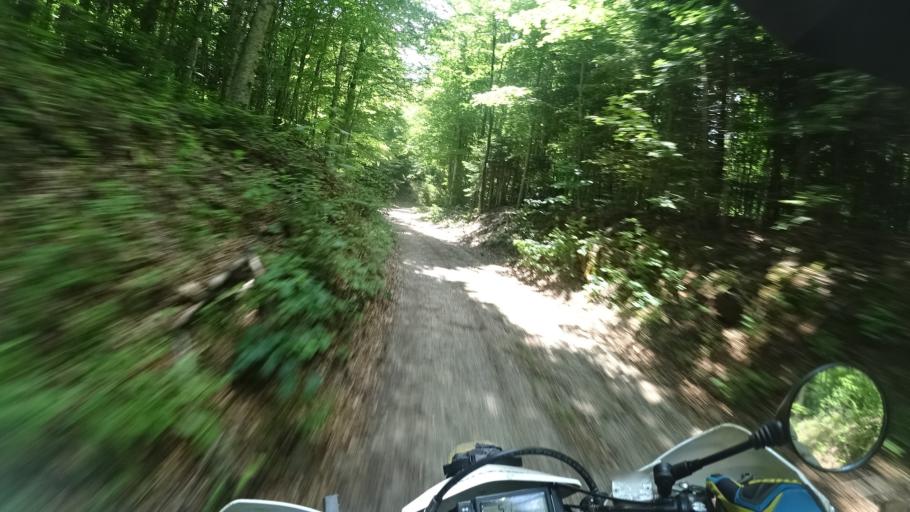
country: HR
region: Zadarska
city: Gracac
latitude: 44.4916
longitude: 15.8739
